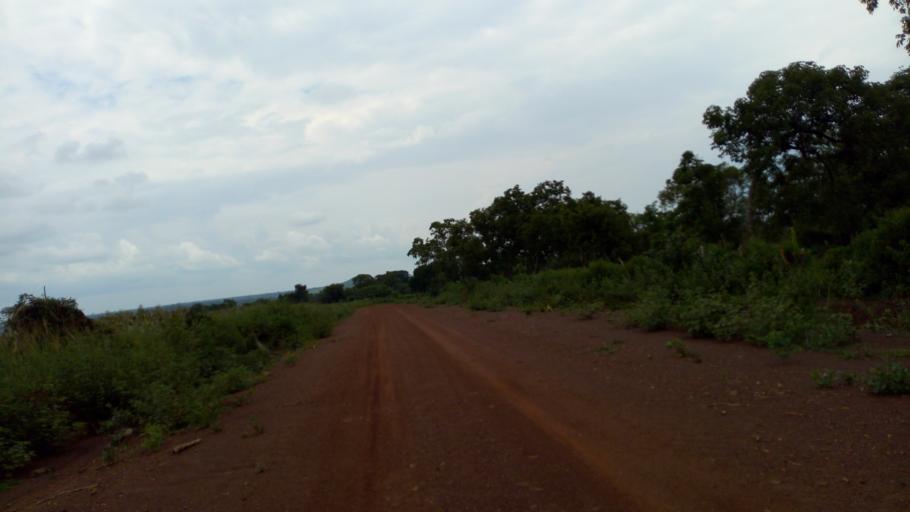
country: UG
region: Western Region
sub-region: Masindi District
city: Masindi
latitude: 1.5436
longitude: 31.7502
